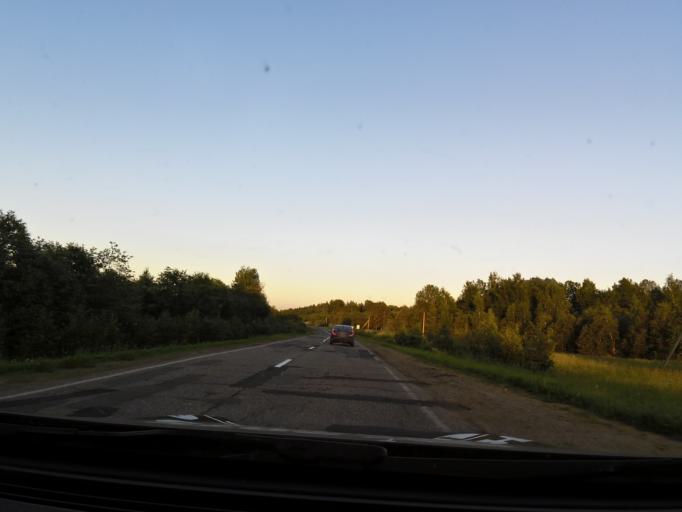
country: RU
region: Jaroslavl
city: Prechistoye
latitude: 58.3880
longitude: 40.4470
